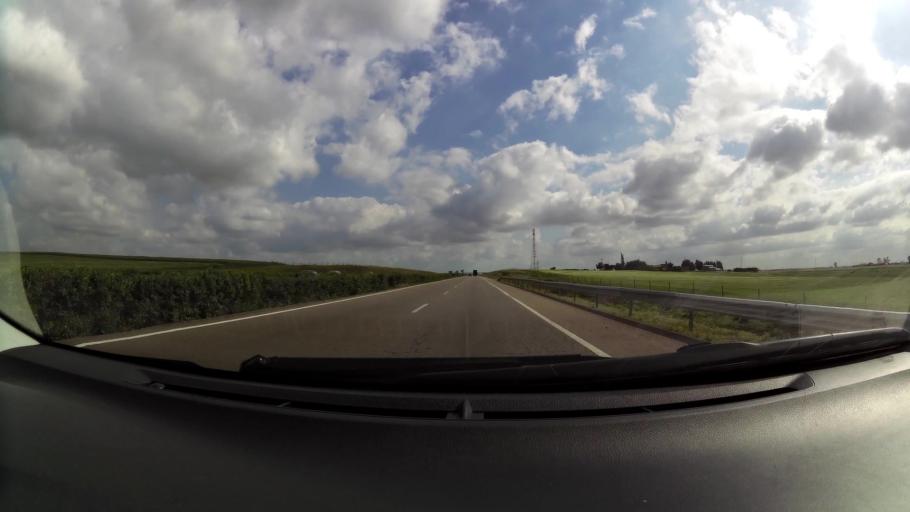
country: MA
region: Chaouia-Ouardigha
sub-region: Settat Province
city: Berrechid
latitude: 33.2139
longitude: -7.5750
